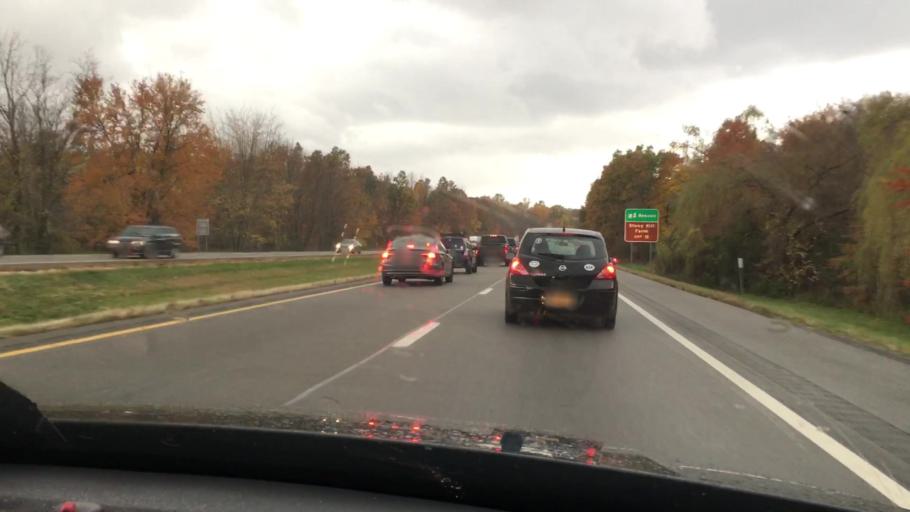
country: US
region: New York
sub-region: Dutchess County
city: Beacon
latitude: 41.5226
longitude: -73.9630
